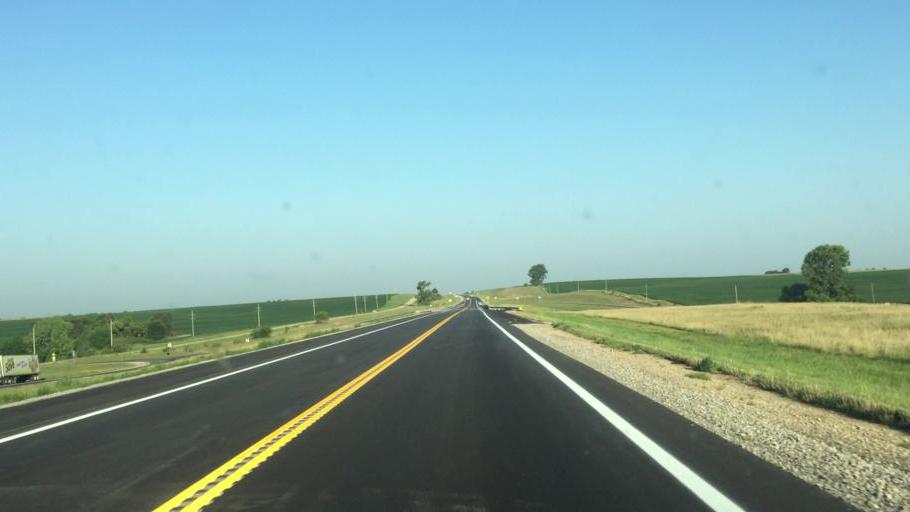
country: US
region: Kansas
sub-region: Brown County
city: Hiawatha
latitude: 39.8414
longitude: -95.4128
